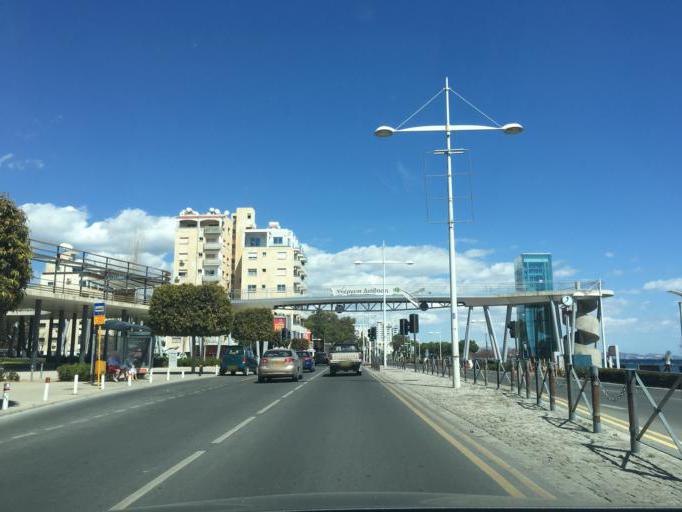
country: CY
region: Limassol
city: Limassol
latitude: 34.6805
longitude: 33.0537
